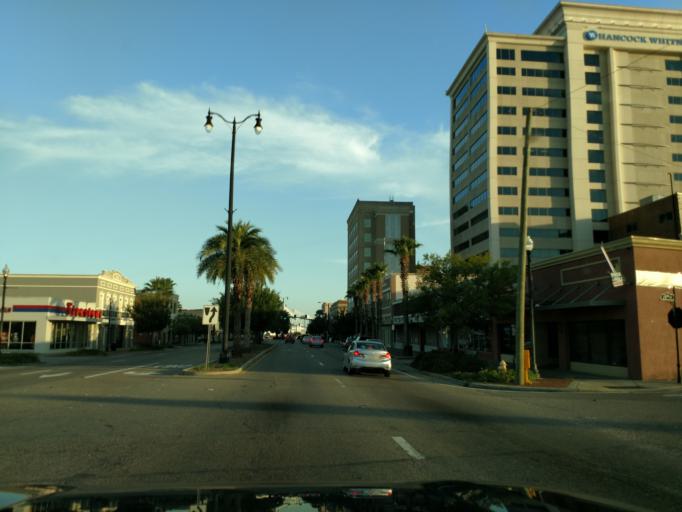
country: US
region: Mississippi
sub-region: Harrison County
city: Gulfport
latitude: 30.3696
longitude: -89.0930
